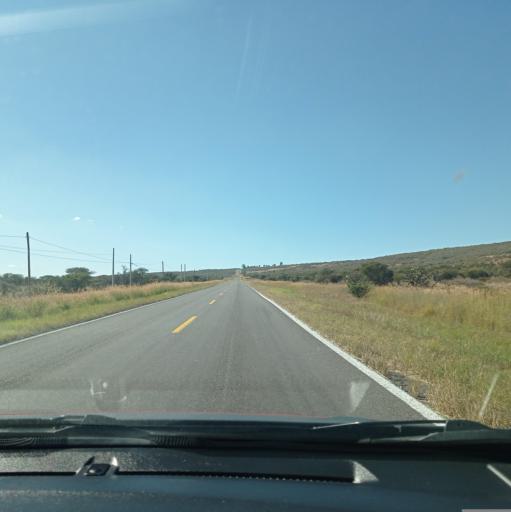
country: MX
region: Jalisco
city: San Miguel el Alto
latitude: 21.0176
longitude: -102.5023
